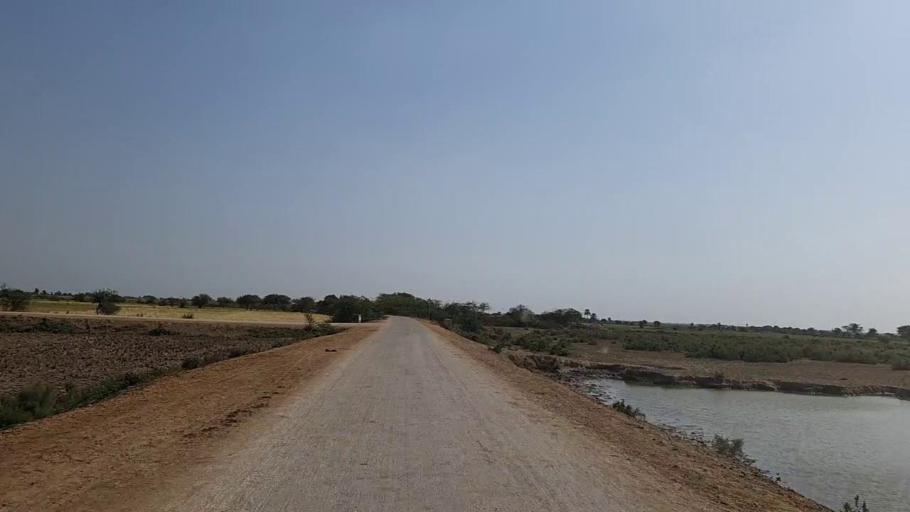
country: PK
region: Sindh
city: Daro Mehar
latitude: 24.7715
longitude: 68.1813
